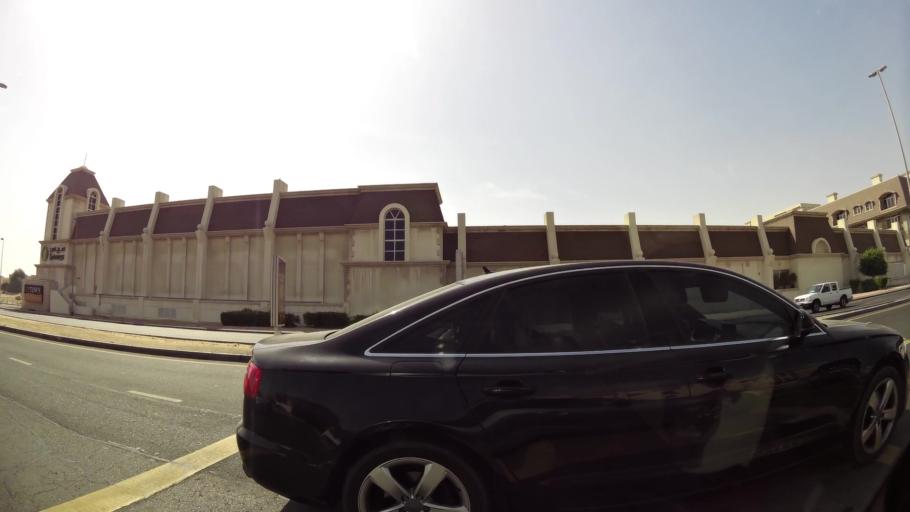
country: AE
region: Ash Shariqah
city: Sharjah
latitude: 25.2254
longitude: 55.4238
